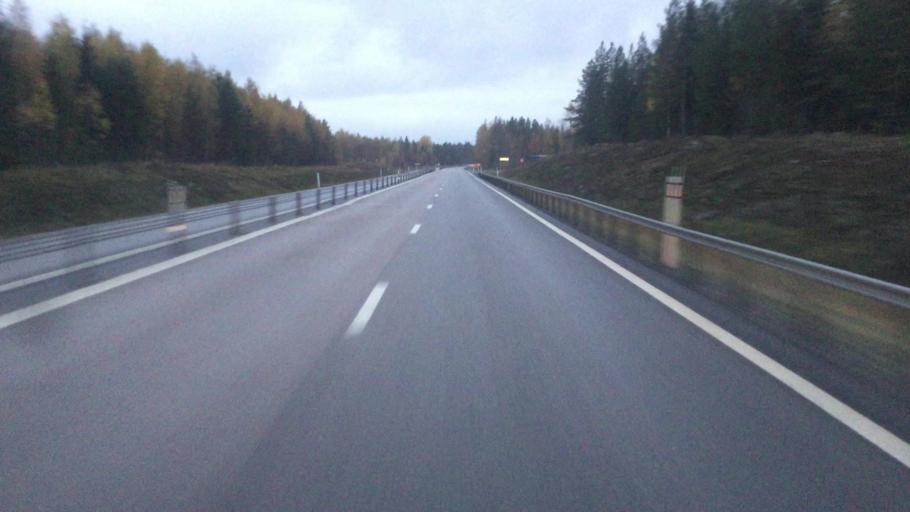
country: SE
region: Vaesterbotten
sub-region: Umea Kommun
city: Saevar
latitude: 63.9710
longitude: 20.7116
